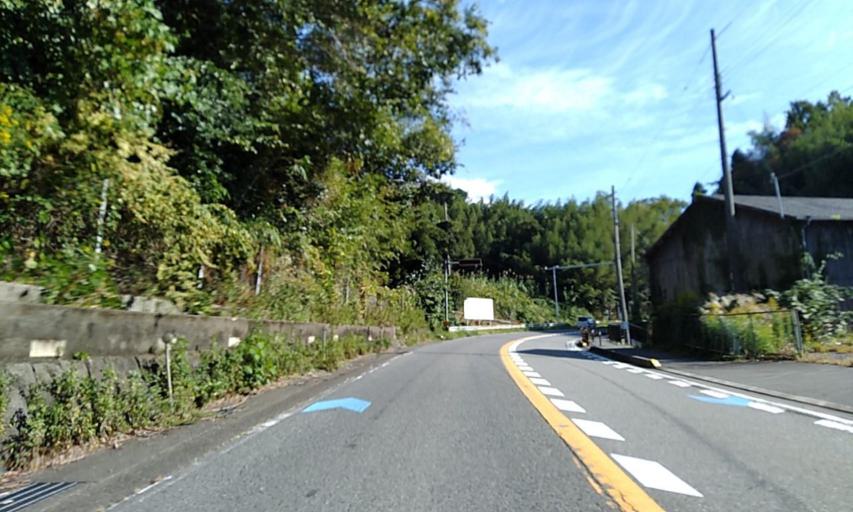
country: JP
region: Wakayama
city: Tanabe
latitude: 33.7813
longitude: 135.2896
